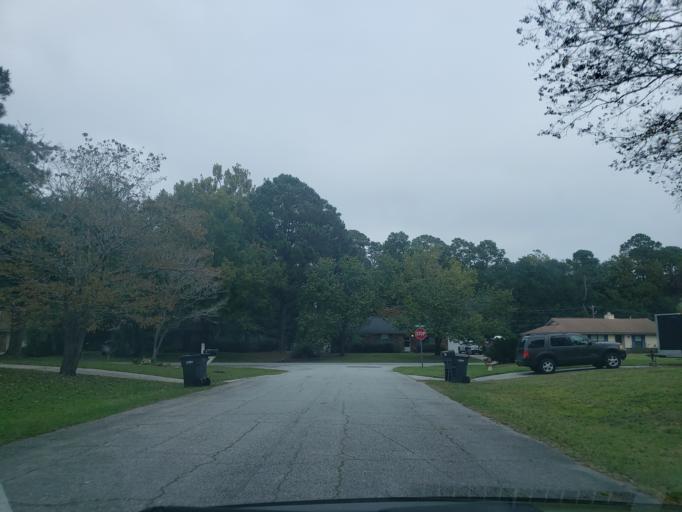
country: US
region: Georgia
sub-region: Chatham County
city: Montgomery
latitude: 31.9530
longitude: -81.1093
